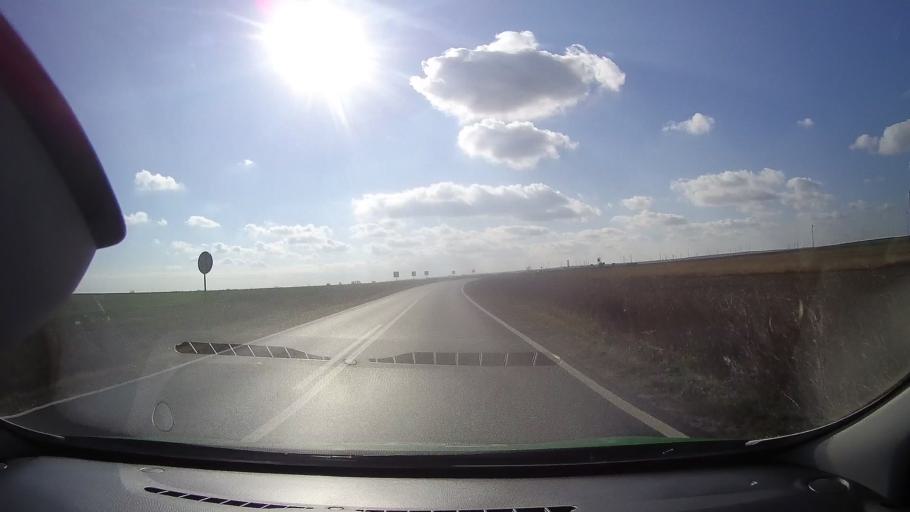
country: RO
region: Constanta
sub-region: Comuna Mihai Viteazu
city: Mihai Viteazu
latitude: 44.6683
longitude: 28.6830
